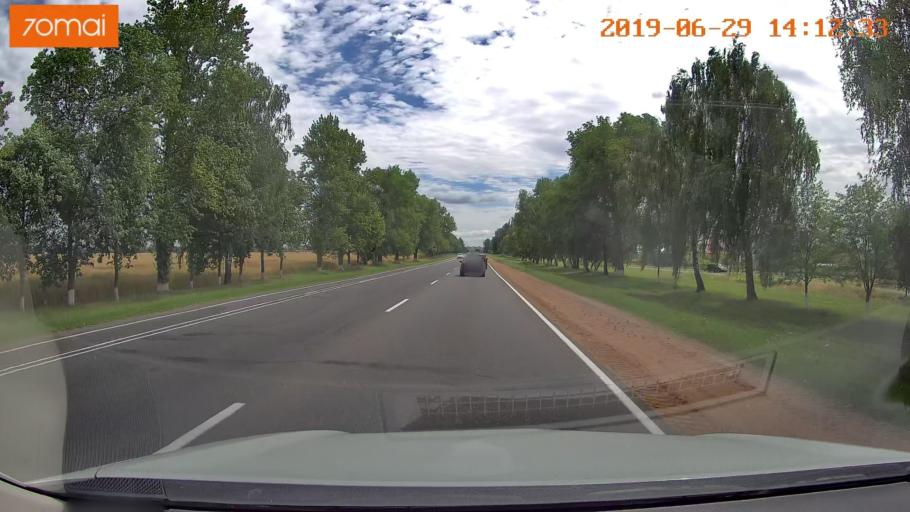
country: BY
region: Minsk
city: Salihorsk
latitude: 52.8091
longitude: 27.5079
